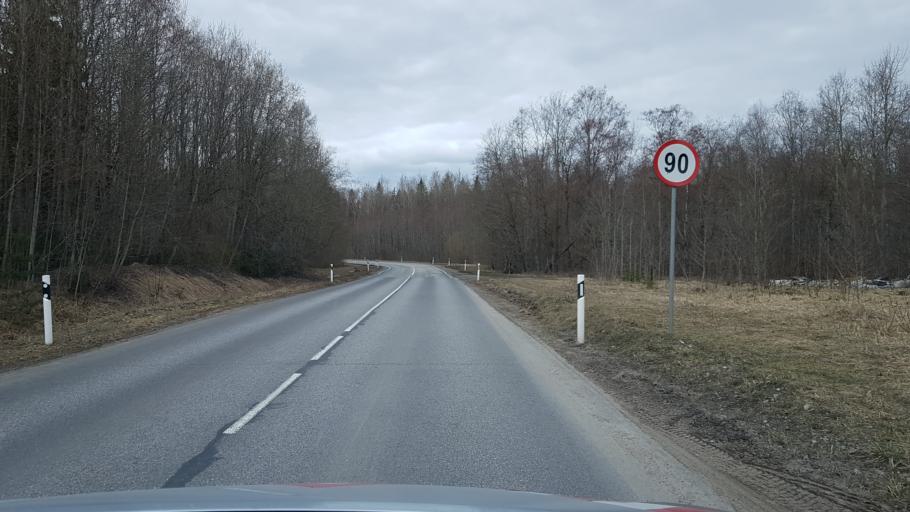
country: EE
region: Ida-Virumaa
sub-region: Narva linn
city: Narva
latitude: 59.3523
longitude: 28.0966
